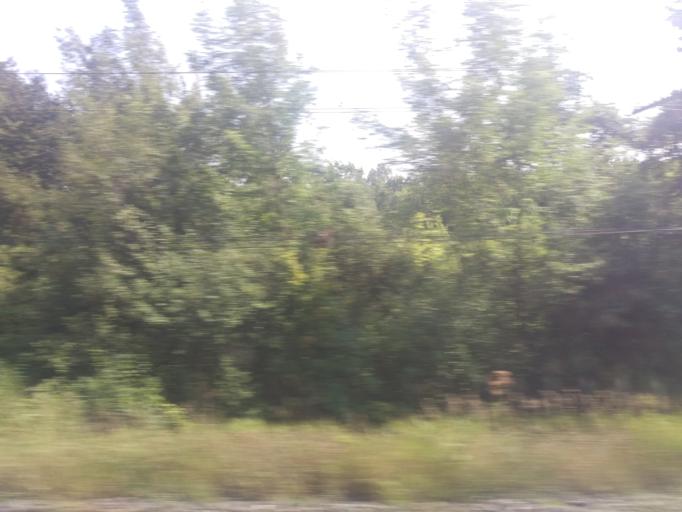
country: CA
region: Ontario
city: Gananoque
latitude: 44.3416
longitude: -76.2825
